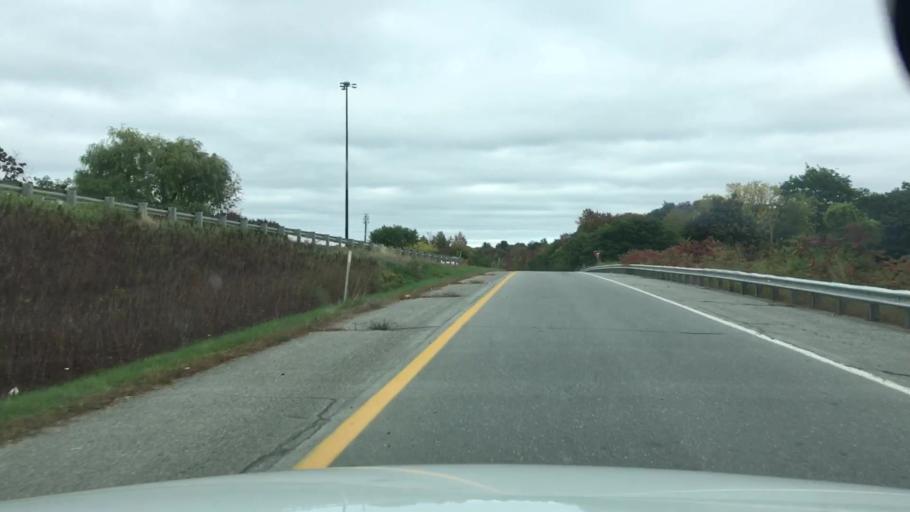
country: US
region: Maine
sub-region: Kennebec County
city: Waterville
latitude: 44.5717
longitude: -69.6385
